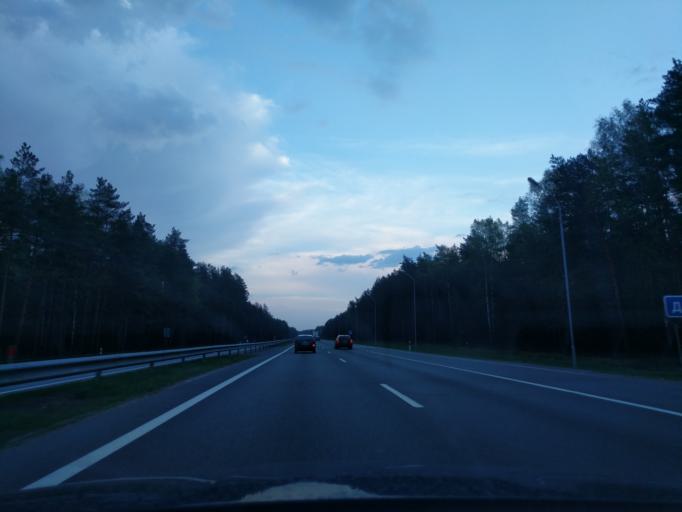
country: BY
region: Minsk
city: Enyerhyetykaw
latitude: 53.5456
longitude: 26.9348
